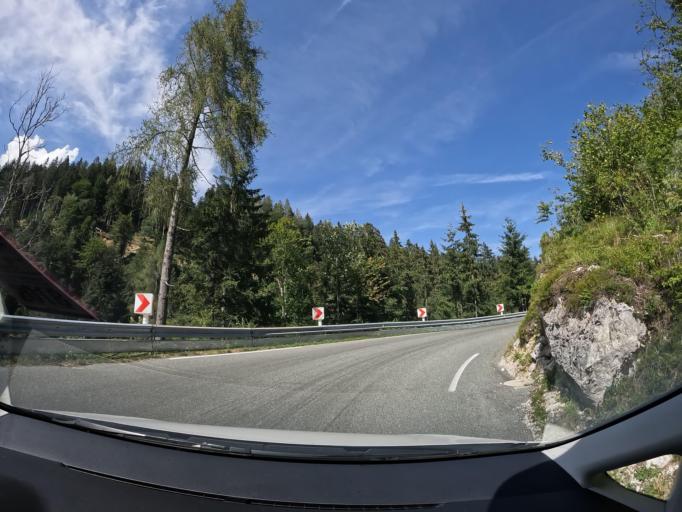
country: AT
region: Carinthia
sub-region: Politischer Bezirk Klagenfurt Land
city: Schiefling am See
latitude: 46.6116
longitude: 14.1053
